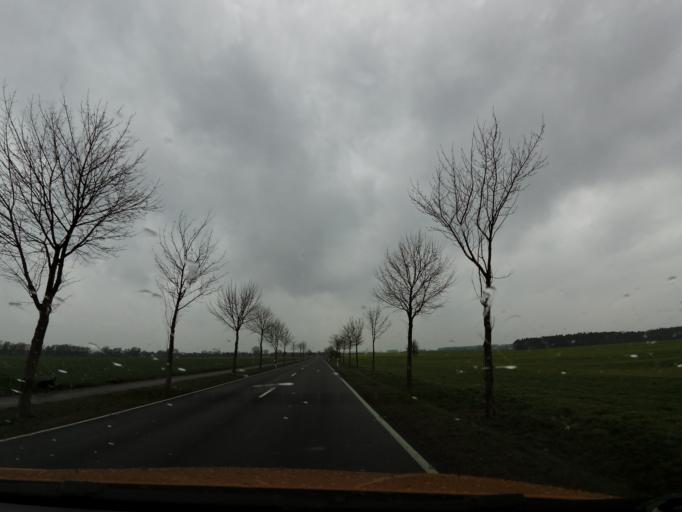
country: DE
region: Brandenburg
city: Ziesar
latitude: 52.2753
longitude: 12.2519
